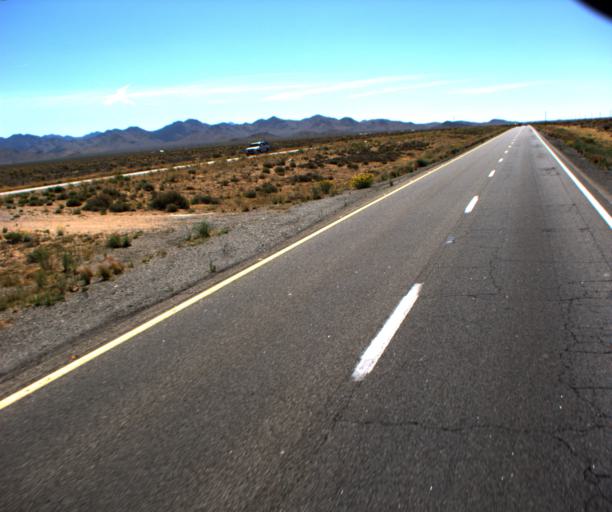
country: US
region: Arizona
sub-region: Mohave County
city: Dolan Springs
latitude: 35.5070
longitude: -114.3370
